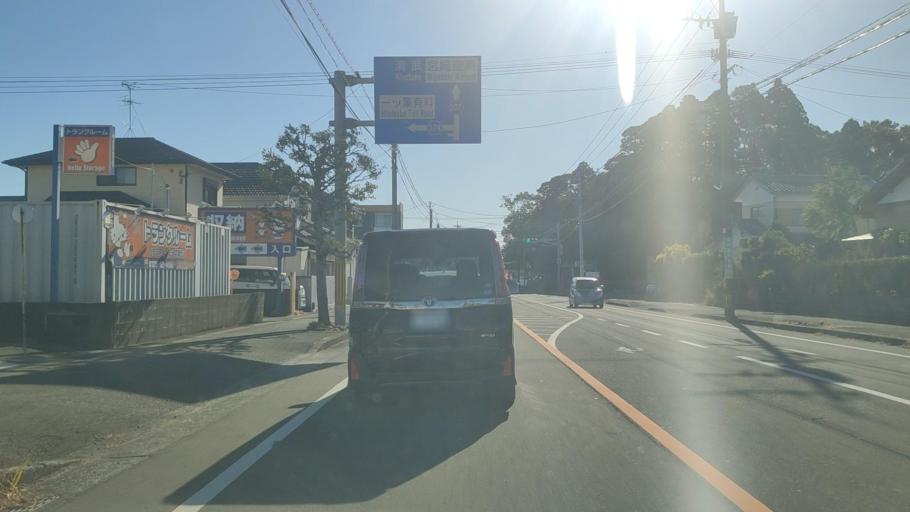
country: JP
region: Miyazaki
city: Miyazaki-shi
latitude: 31.8875
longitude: 131.4292
